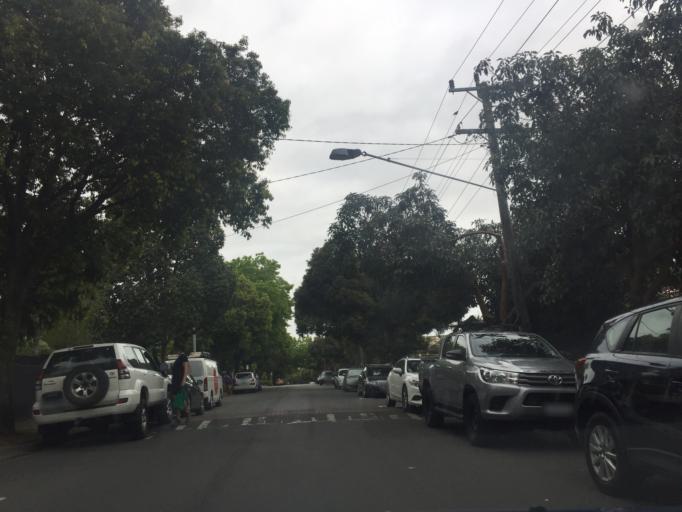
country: AU
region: Victoria
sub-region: Boroondara
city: Hawthorn East
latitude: -37.8159
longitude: 145.0426
